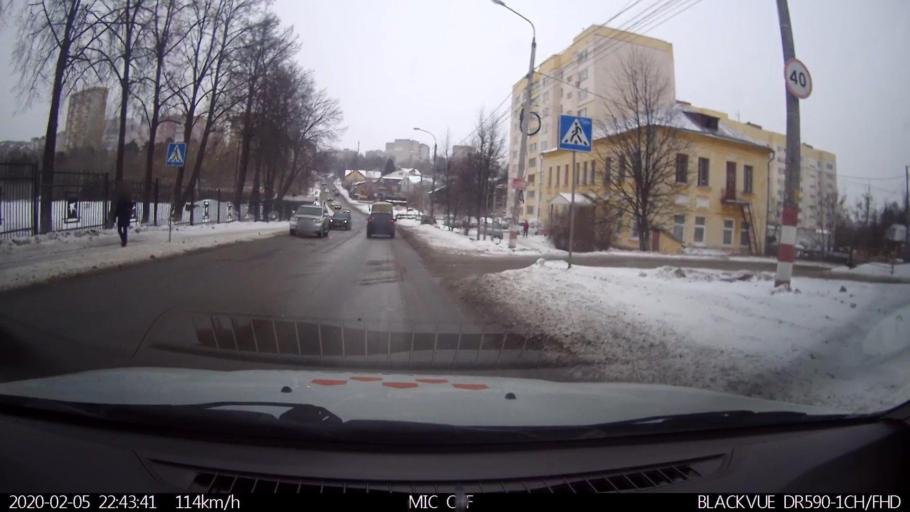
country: RU
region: Nizjnij Novgorod
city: Imeni Stepana Razina
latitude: 54.7118
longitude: 44.3840
